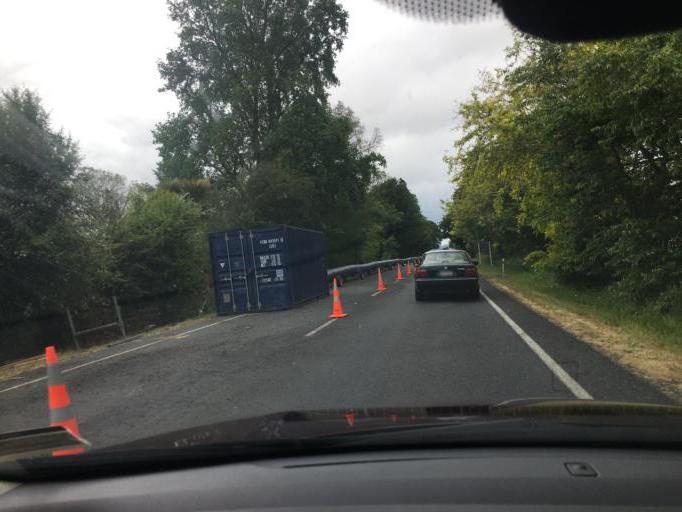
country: NZ
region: Waikato
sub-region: Waipa District
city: Cambridge
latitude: -37.9229
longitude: 175.4356
